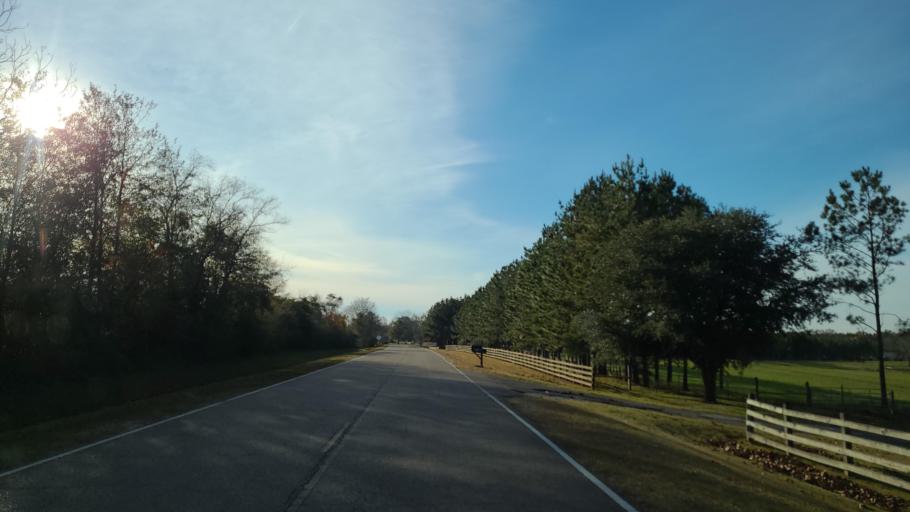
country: US
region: Mississippi
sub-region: Lamar County
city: Purvis
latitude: 31.1656
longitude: -89.3134
